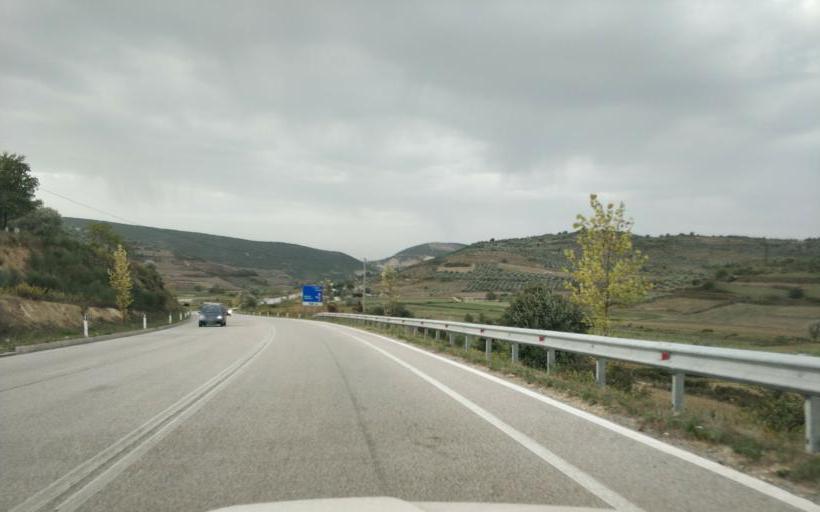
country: AL
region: Fier
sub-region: Rrethi i Mallakastres
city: Fratar
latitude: 40.4952
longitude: 19.8284
